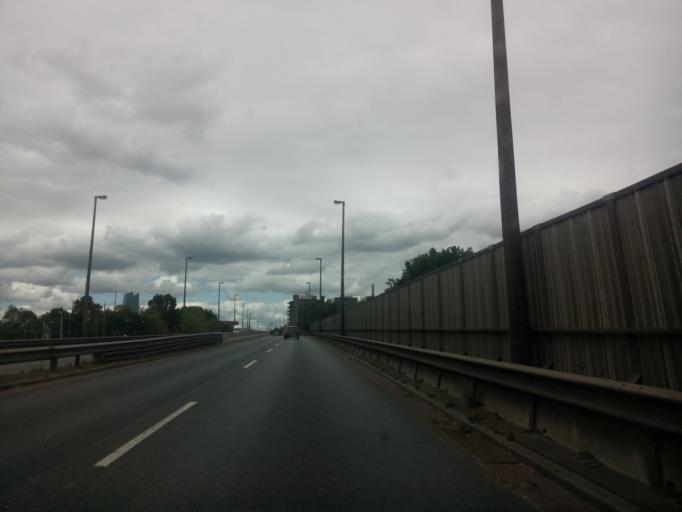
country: DE
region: Bremen
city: Bremen
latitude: 53.0733
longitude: 8.7857
